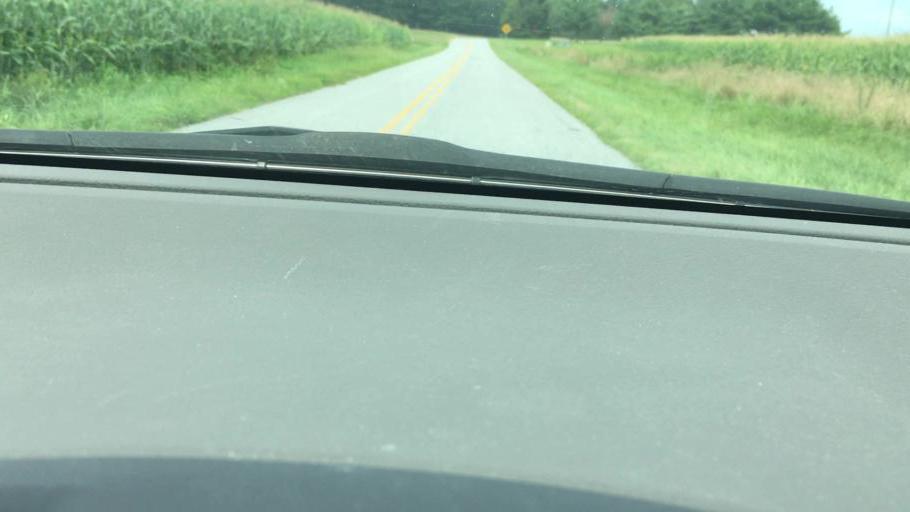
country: US
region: Maryland
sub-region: Worcester County
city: Pocomoke City
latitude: 38.0621
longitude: -75.5047
